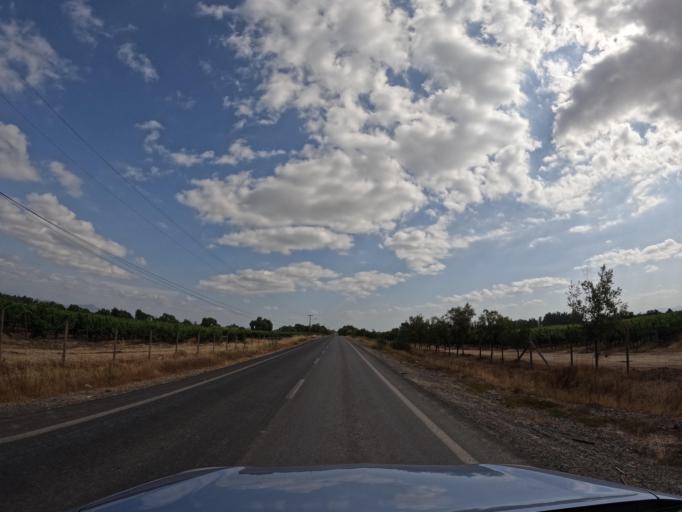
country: CL
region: Maule
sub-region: Provincia de Curico
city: Molina
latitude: -35.1776
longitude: -71.2936
